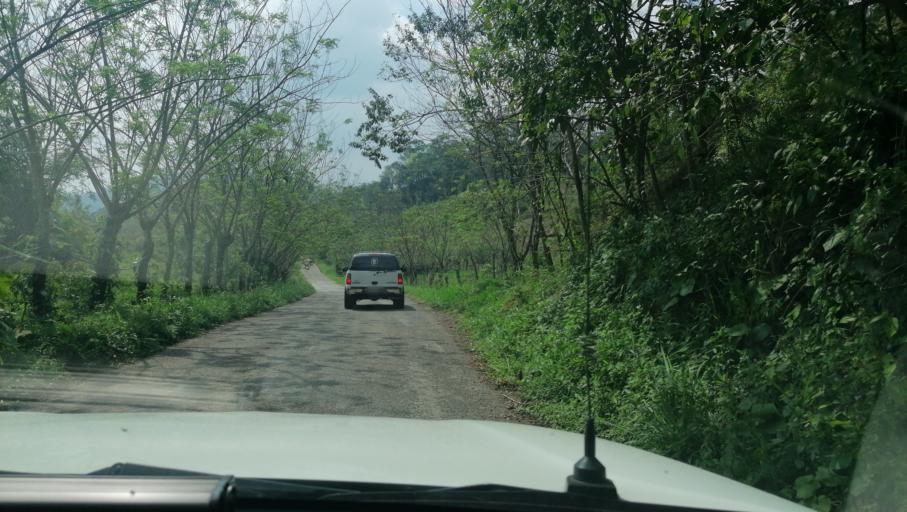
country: MX
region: Chiapas
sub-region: Francisco Leon
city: San Miguel la Sardina
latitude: 17.2341
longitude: -93.3368
